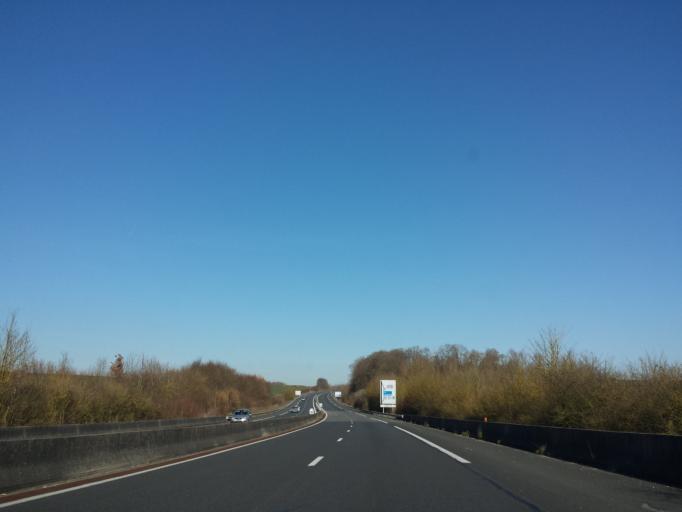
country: FR
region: Picardie
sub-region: Departement de l'Oise
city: Breteuil
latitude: 49.5817
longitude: 2.2045
